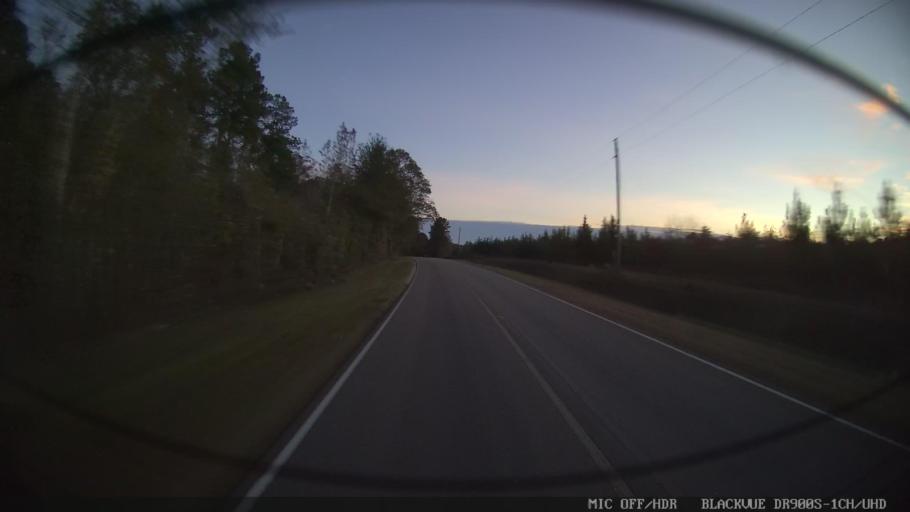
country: US
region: Mississippi
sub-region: Perry County
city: New Augusta
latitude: 31.1196
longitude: -89.1969
